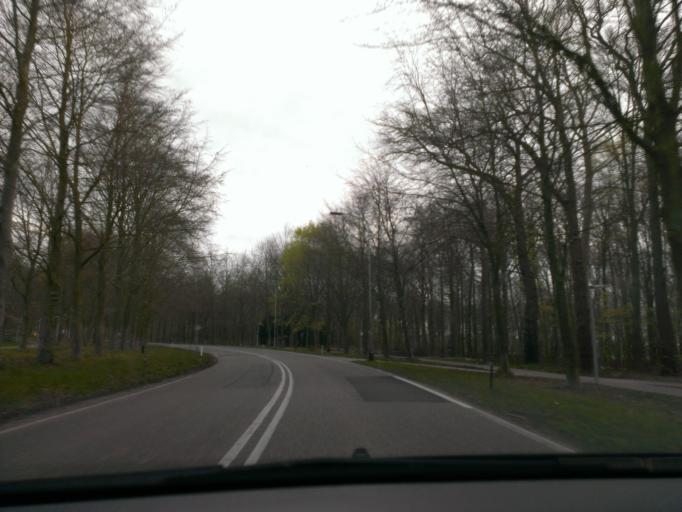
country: NL
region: Gelderland
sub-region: Gemeente Voorst
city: Twello
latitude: 52.2221
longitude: 6.1124
